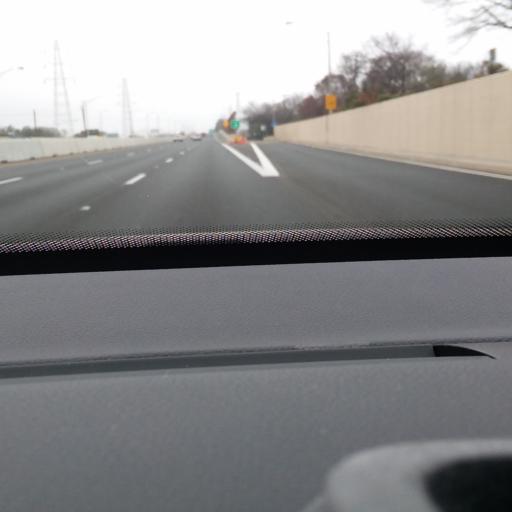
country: US
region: Texas
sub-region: Dallas County
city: University Park
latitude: 32.8988
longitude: -96.8096
